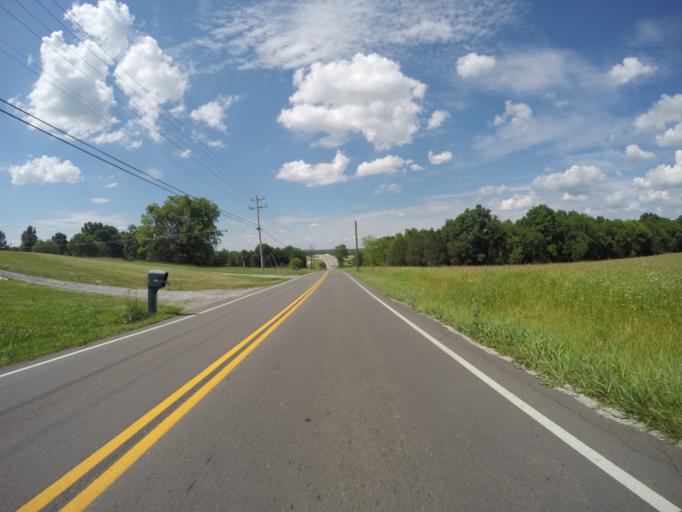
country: US
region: Tennessee
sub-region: Wilson County
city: Rural Hill
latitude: 36.1733
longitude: -86.4573
